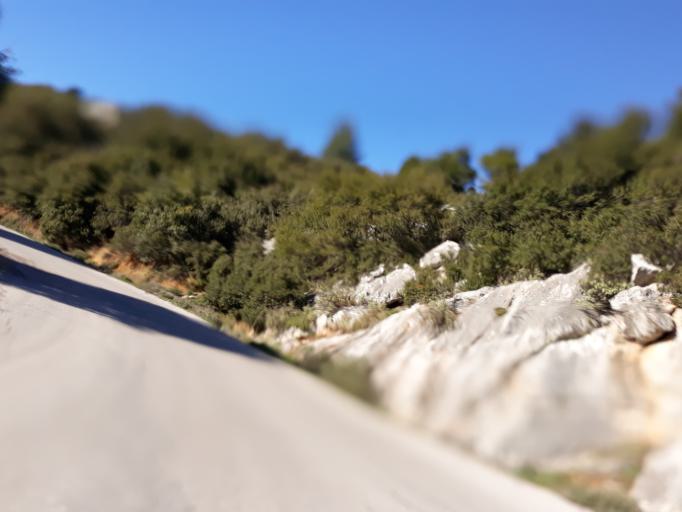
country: GR
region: Attica
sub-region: Nomarchia Dytikis Attikis
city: Fyli
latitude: 38.1406
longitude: 23.6480
